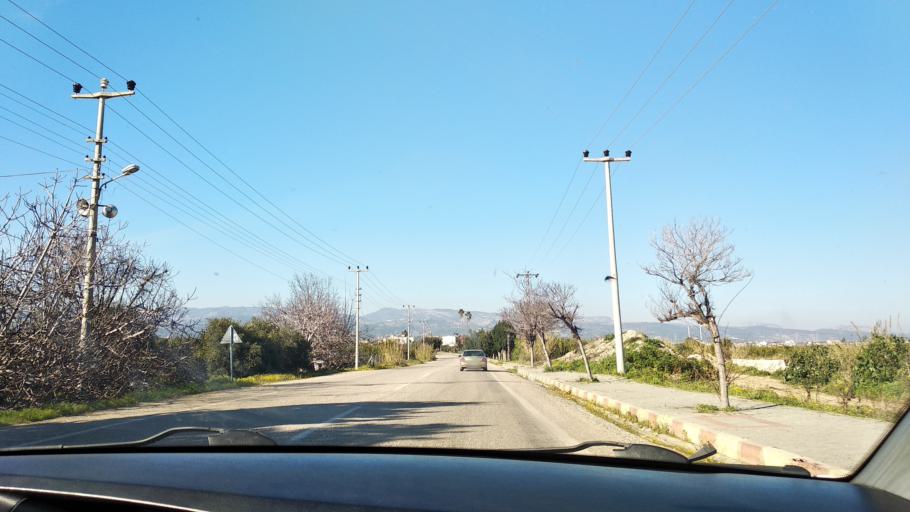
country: TR
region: Mersin
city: Tomuk
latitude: 36.6534
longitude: 34.3680
